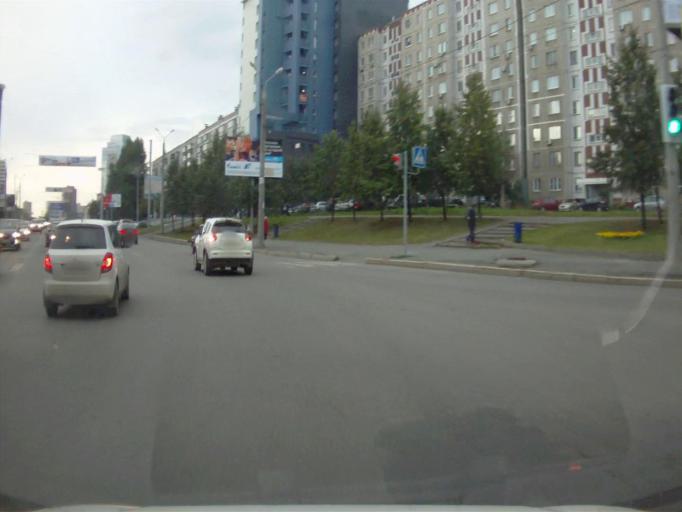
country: RU
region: Chelyabinsk
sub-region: Gorod Chelyabinsk
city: Chelyabinsk
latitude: 55.1531
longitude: 61.3816
